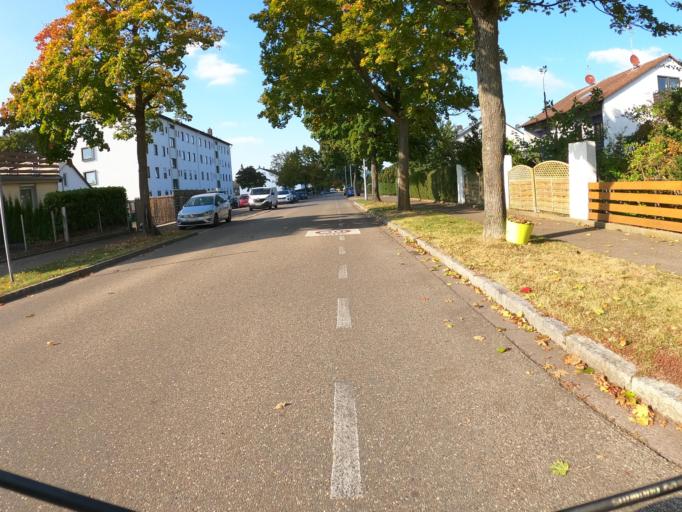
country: DE
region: Bavaria
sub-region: Swabia
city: Leipheim
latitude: 48.4495
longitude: 10.2289
